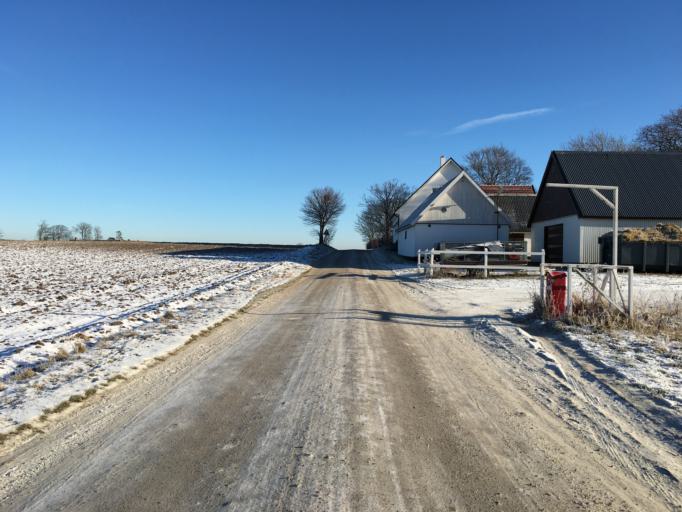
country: SE
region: Skane
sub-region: Vellinge Kommun
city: Vellinge
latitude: 55.4390
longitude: 13.0001
